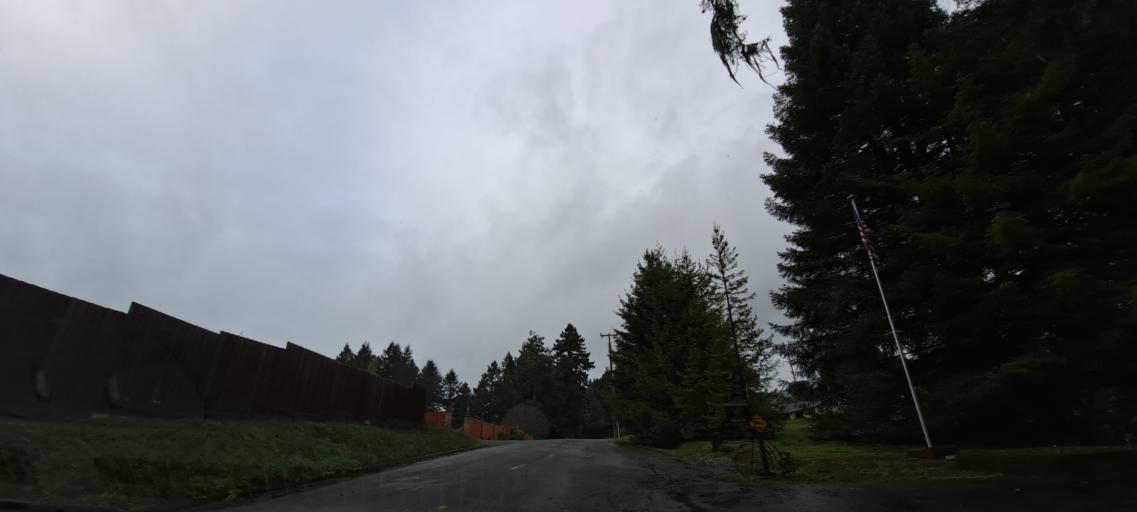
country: US
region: California
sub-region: Humboldt County
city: Fortuna
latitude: 40.6007
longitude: -124.1402
